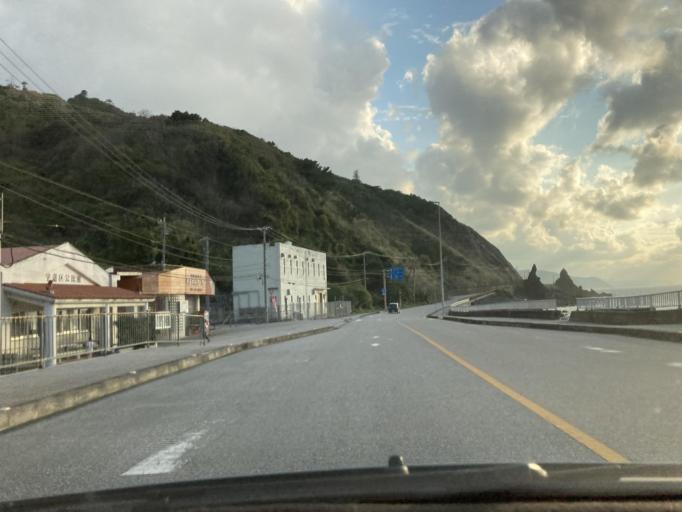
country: JP
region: Okinawa
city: Nago
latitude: 26.8087
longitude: 128.2342
